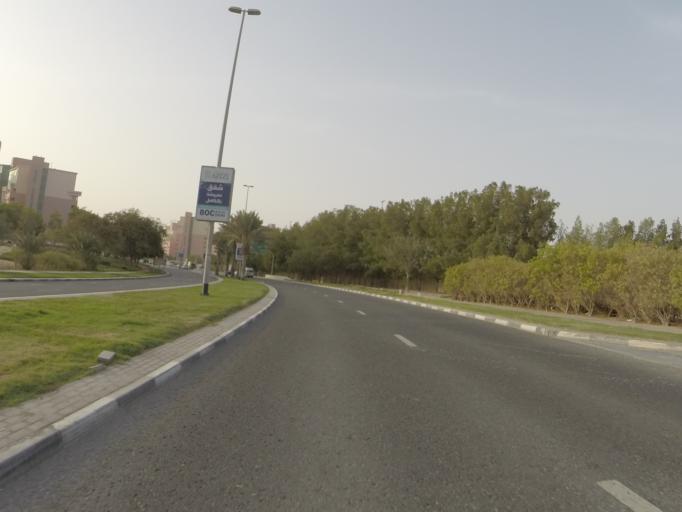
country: AE
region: Dubai
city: Dubai
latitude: 25.0497
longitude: 55.1269
